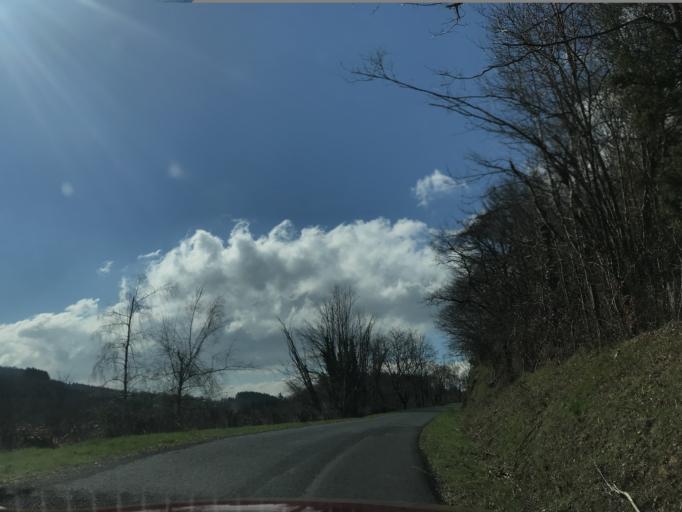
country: FR
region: Auvergne
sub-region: Departement du Puy-de-Dome
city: Escoutoux
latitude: 45.8079
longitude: 3.6036
